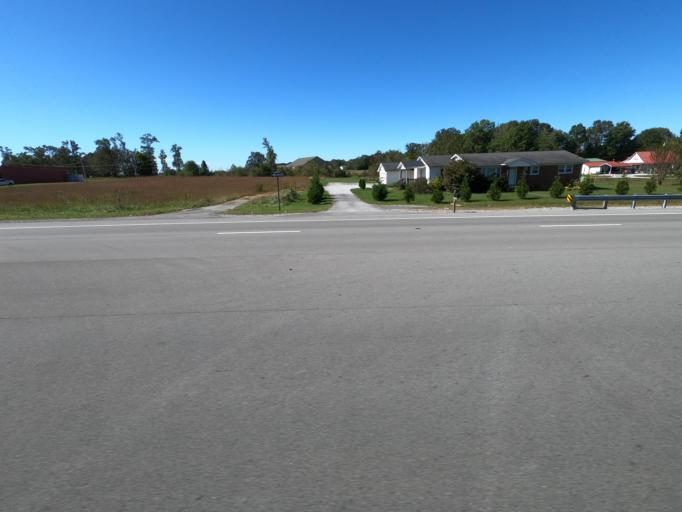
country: US
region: Tennessee
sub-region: Maury County
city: Mount Pleasant
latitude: 35.4325
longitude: -87.2808
